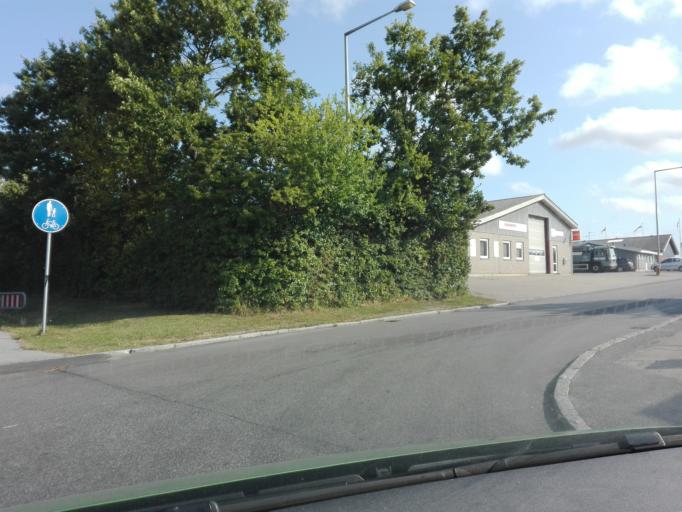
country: DK
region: Central Jutland
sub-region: Arhus Kommune
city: Lystrup
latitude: 56.2056
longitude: 10.2304
